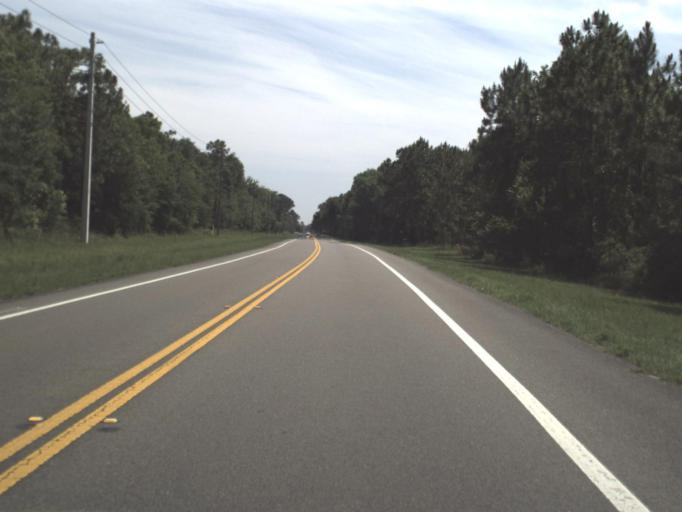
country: US
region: Florida
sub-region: Nassau County
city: Yulee
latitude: 30.5443
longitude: -81.6217
